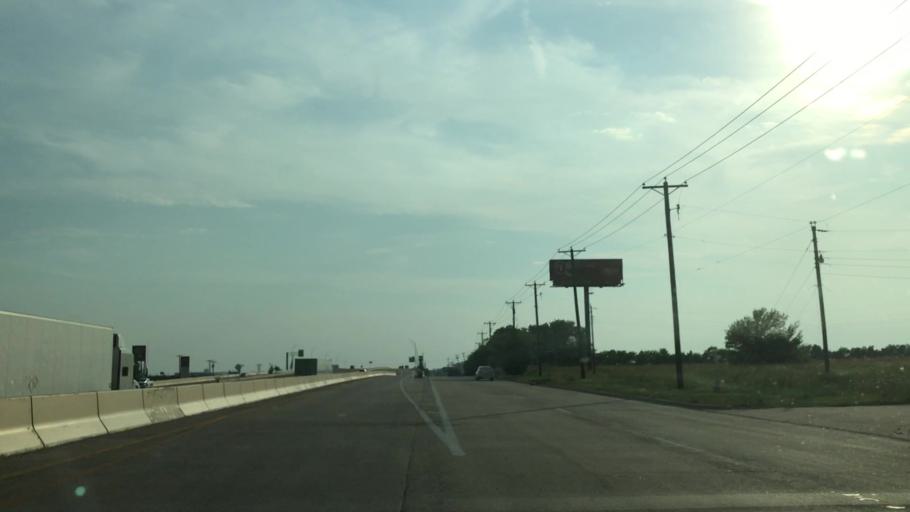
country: US
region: Texas
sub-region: Rockwall County
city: Rockwall
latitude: 32.9175
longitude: -96.4282
